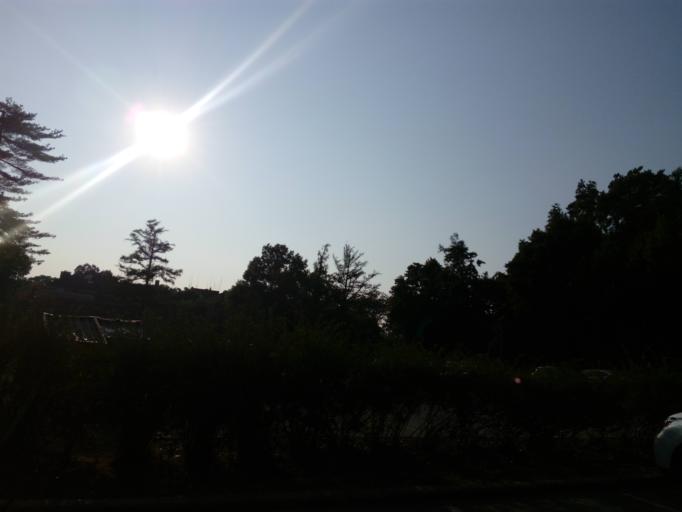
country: US
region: New York
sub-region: Nassau County
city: Glen Cove
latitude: 40.8709
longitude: -73.6203
